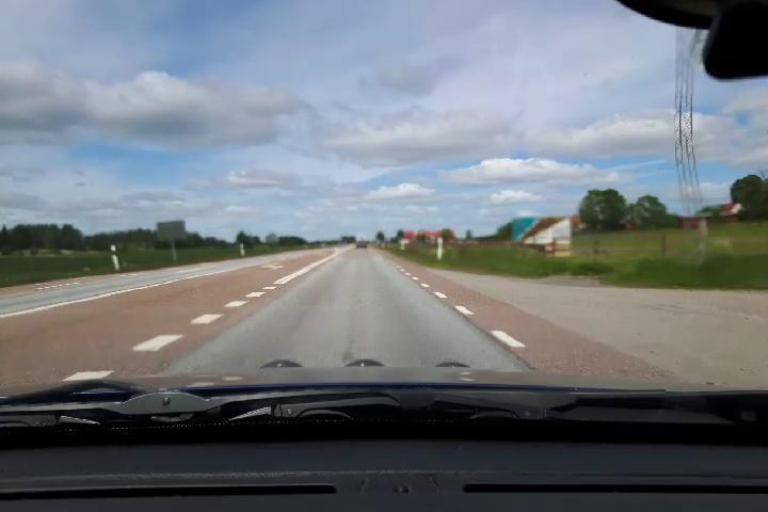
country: SE
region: Uppsala
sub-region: Uppsala Kommun
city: Gamla Uppsala
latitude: 59.9348
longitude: 17.5957
